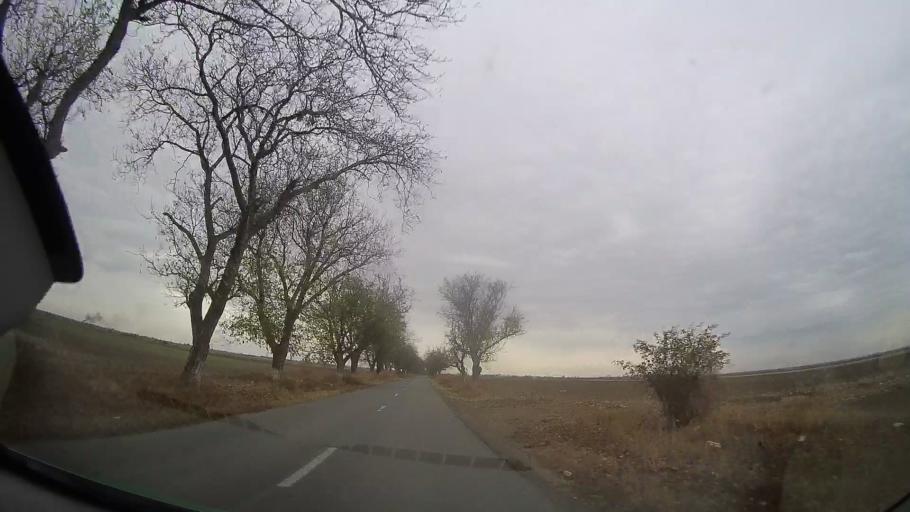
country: RO
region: Prahova
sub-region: Comuna Fantanele
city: Fantanele
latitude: 45.0134
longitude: 26.4090
